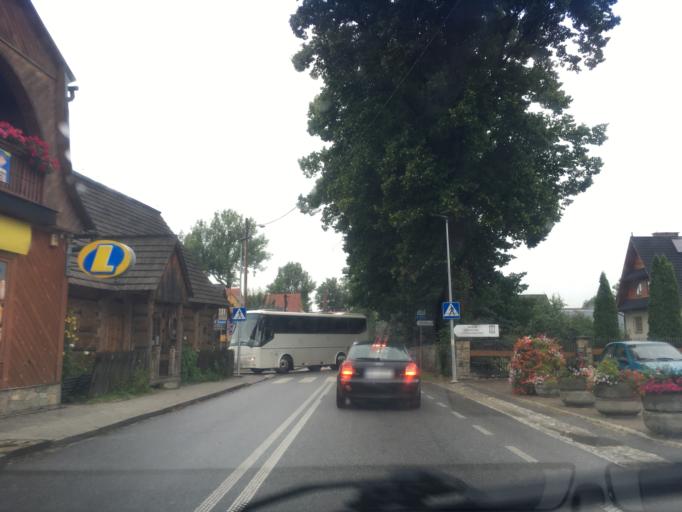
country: PL
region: Lesser Poland Voivodeship
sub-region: Powiat nowotarski
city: Czarny Dunajec
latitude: 49.3715
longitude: 19.8167
